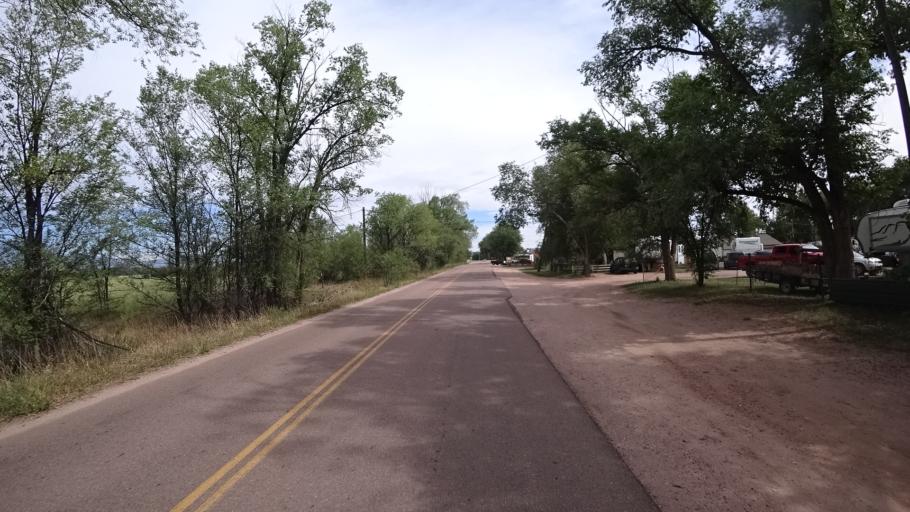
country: US
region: Colorado
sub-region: El Paso County
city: Security-Widefield
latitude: 38.7476
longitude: -104.7434
